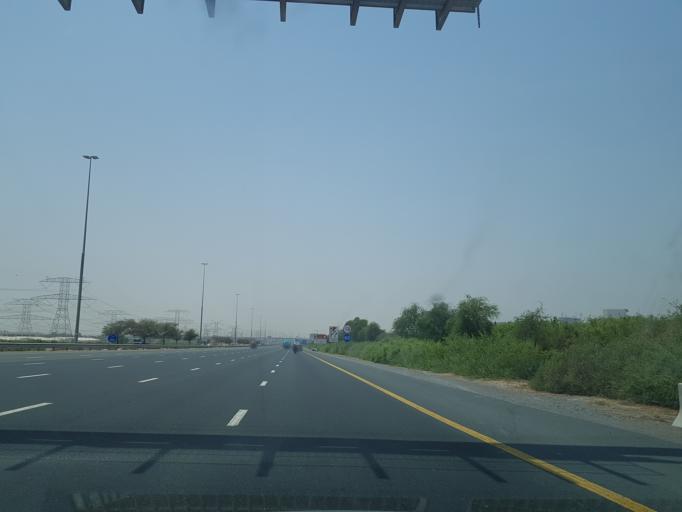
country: AE
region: Dubai
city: Dubai
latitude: 25.0964
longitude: 55.4066
